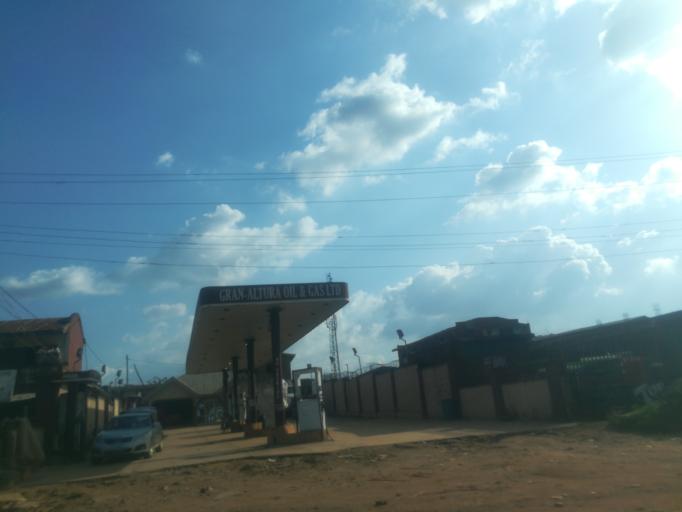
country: NG
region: Oyo
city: Ibadan
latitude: 7.3907
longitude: 3.9737
